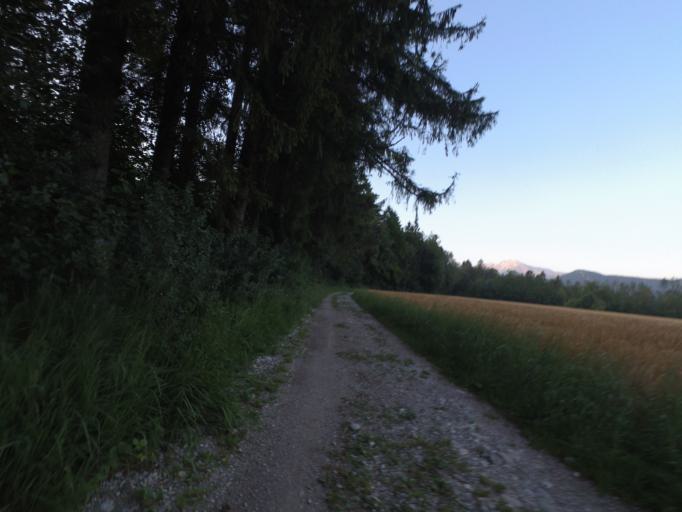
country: AT
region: Salzburg
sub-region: Politischer Bezirk Salzburg-Umgebung
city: Elsbethen
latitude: 47.7376
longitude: 13.0784
